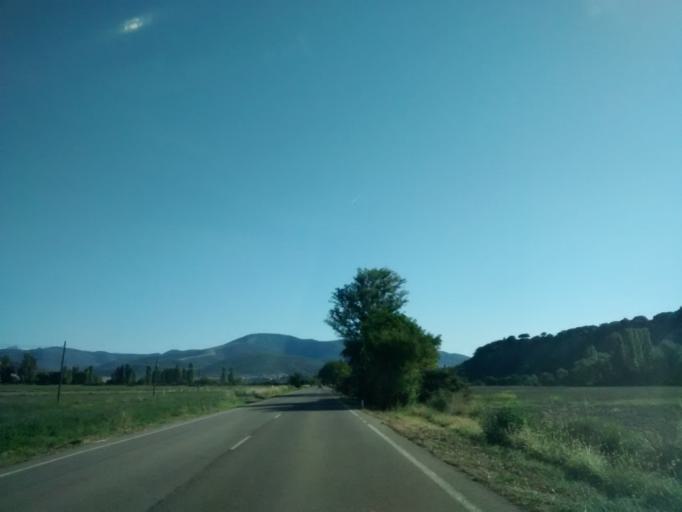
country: ES
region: Aragon
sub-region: Provincia de Huesca
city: Bailo
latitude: 42.5730
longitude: -0.7650
